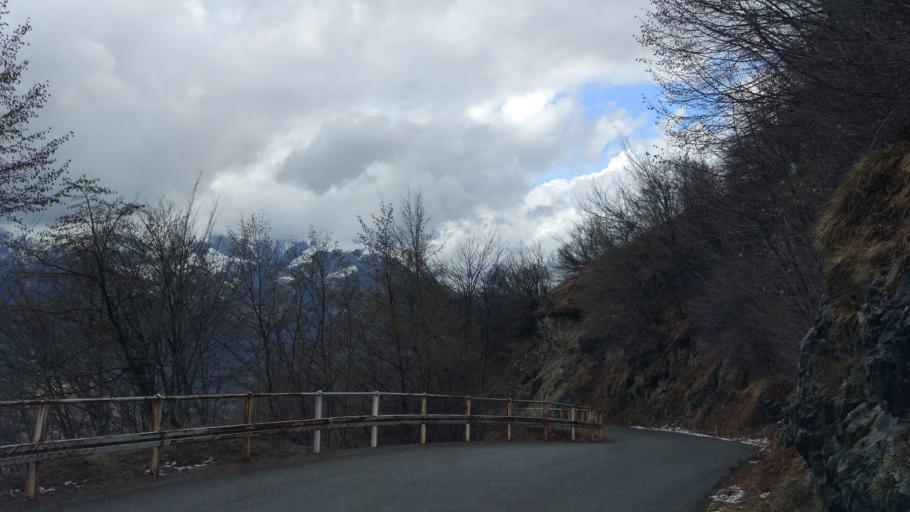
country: IT
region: Lombardy
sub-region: Provincia di Lecco
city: Moggio
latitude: 45.9167
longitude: 9.4933
